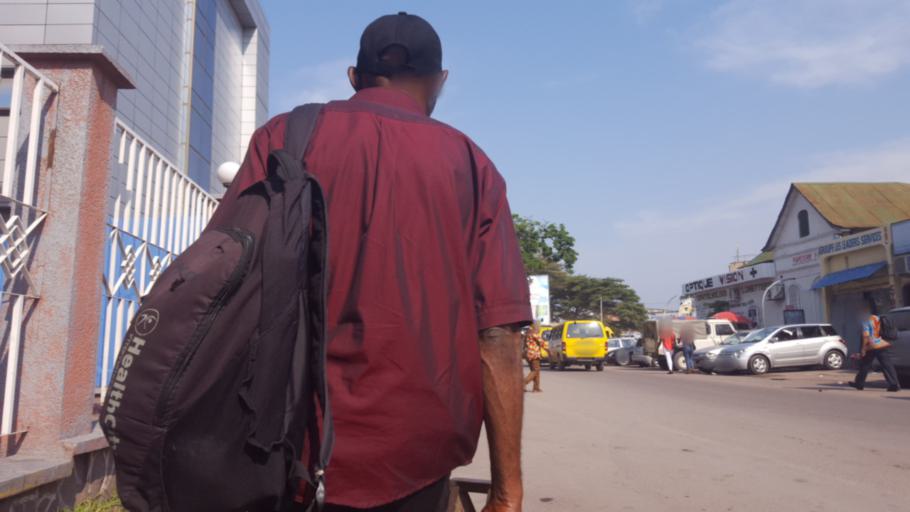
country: CD
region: Kinshasa
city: Kinshasa
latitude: -4.3065
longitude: 15.3082
